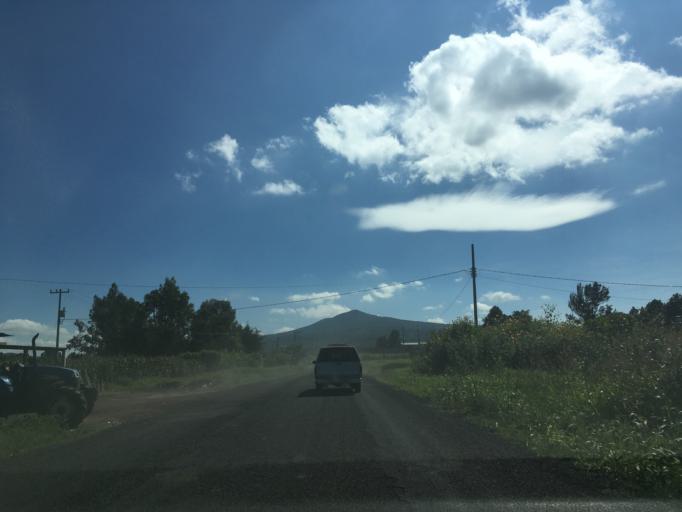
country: MX
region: Mexico
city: Tlazazalca
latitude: 19.9723
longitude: -102.0681
